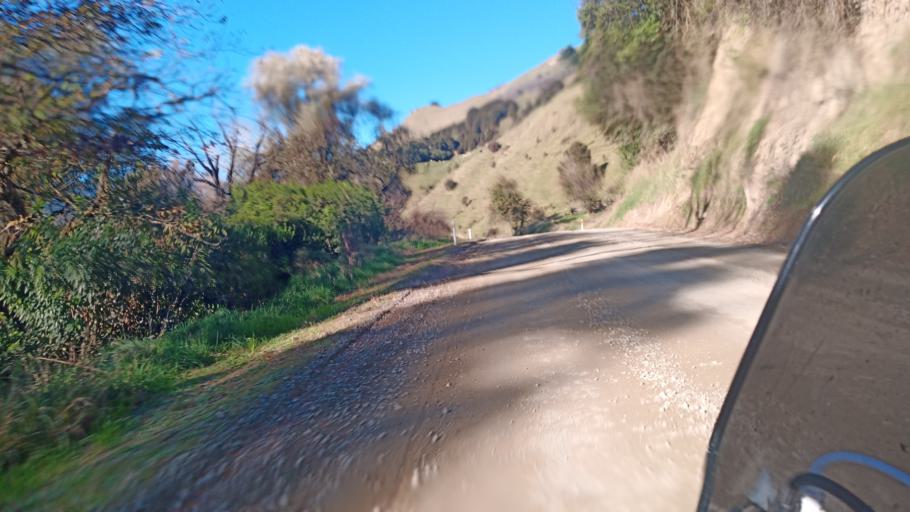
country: NZ
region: Hawke's Bay
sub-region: Wairoa District
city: Wairoa
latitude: -38.8474
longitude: 177.1659
